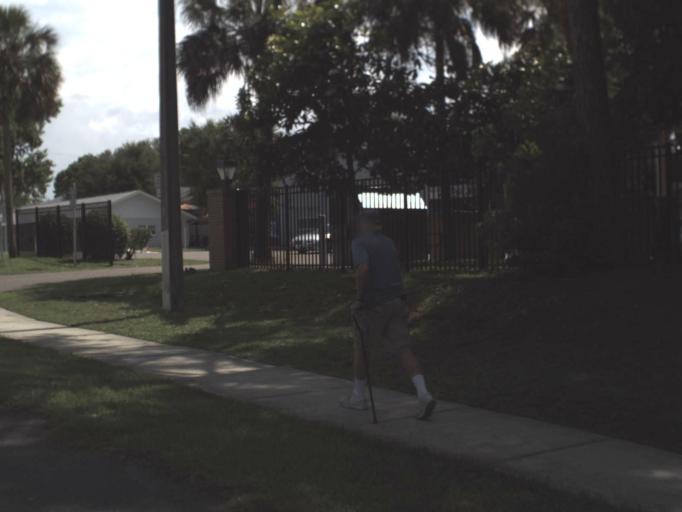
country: US
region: Florida
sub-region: Alachua County
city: Gainesville
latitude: 29.6228
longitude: -82.3395
